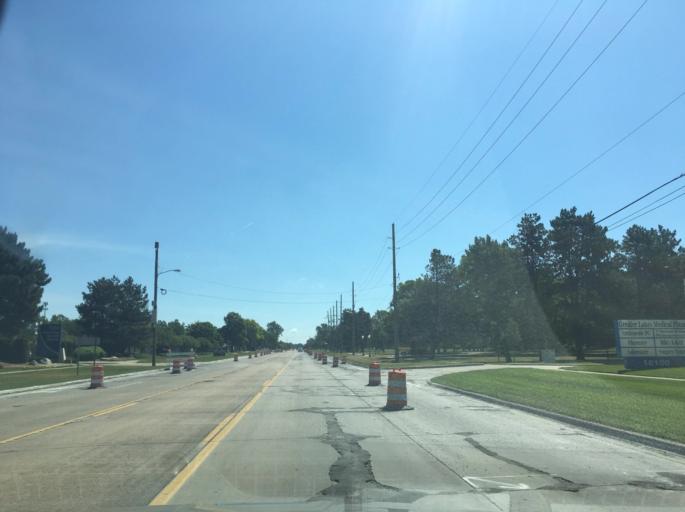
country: US
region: Michigan
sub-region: Macomb County
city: Clinton
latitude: 42.6127
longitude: -82.9619
